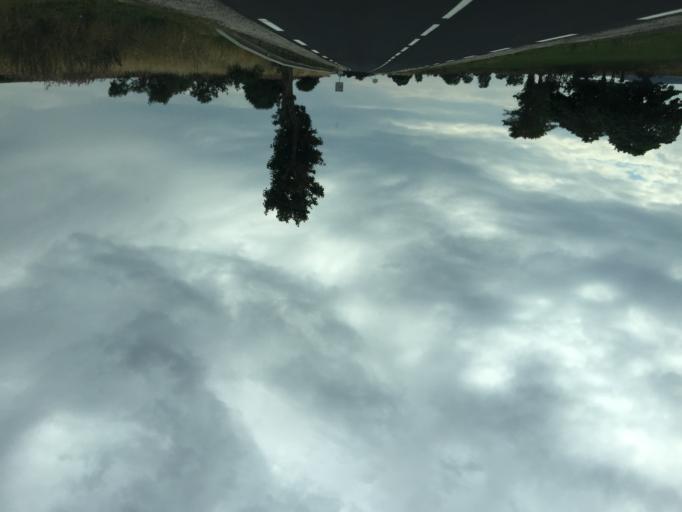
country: FR
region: Auvergne
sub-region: Departement de la Haute-Loire
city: Solignac-sur-Loire
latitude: 44.8682
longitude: 3.8487
